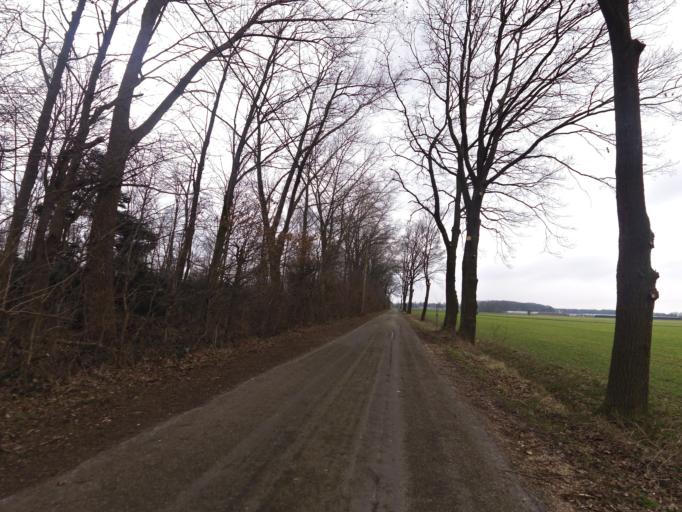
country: NL
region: Gelderland
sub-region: Oude IJsselstreek
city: Gendringen
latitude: 51.8673
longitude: 6.4044
